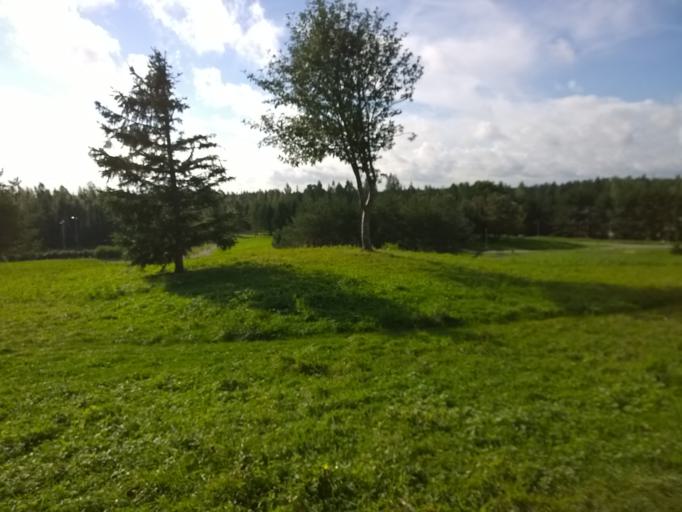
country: FI
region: Pirkanmaa
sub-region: Tampere
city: Tampere
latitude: 61.4445
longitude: 23.8663
